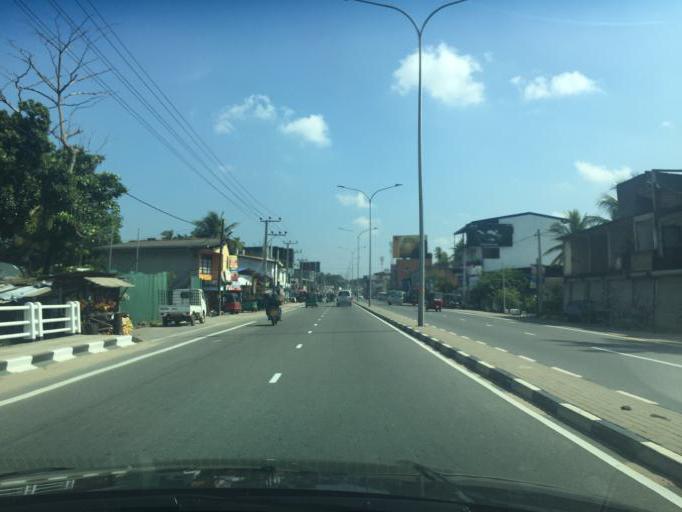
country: LK
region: Western
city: Maharagama
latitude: 6.8225
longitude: 79.9151
